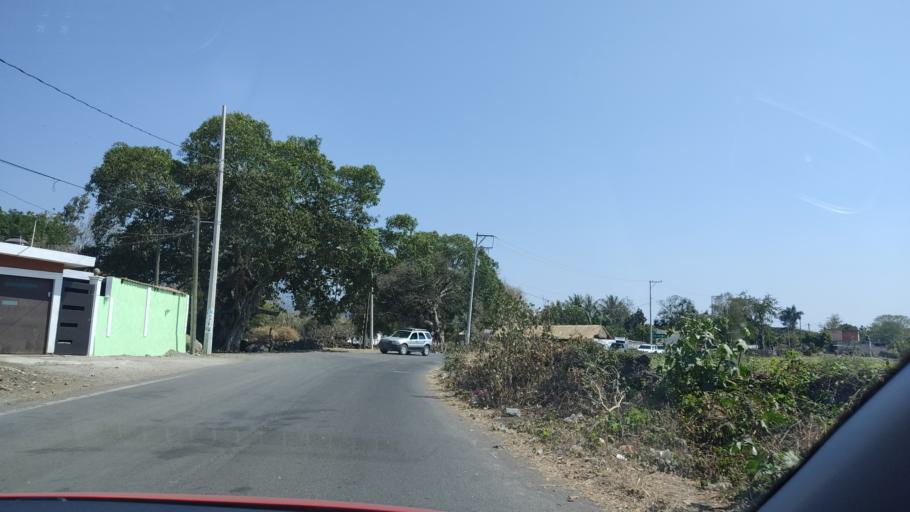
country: MX
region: Nayarit
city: Puga
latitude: 21.5304
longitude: -104.8070
